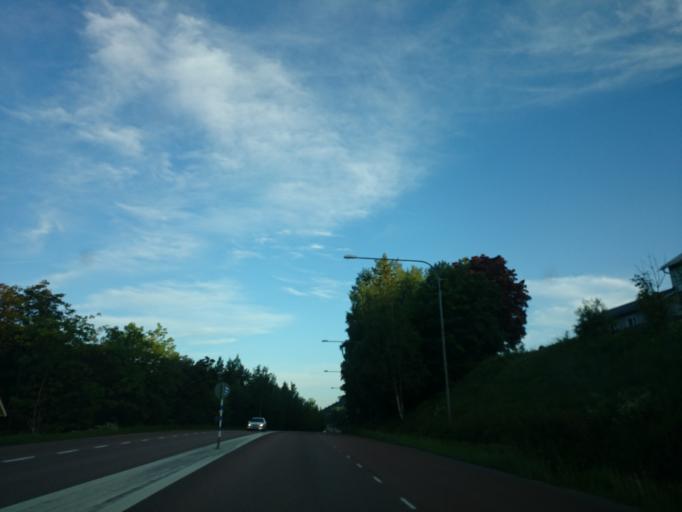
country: SE
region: Vaesternorrland
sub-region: Sundsvalls Kommun
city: Stockvik
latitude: 62.3234
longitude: 17.3683
